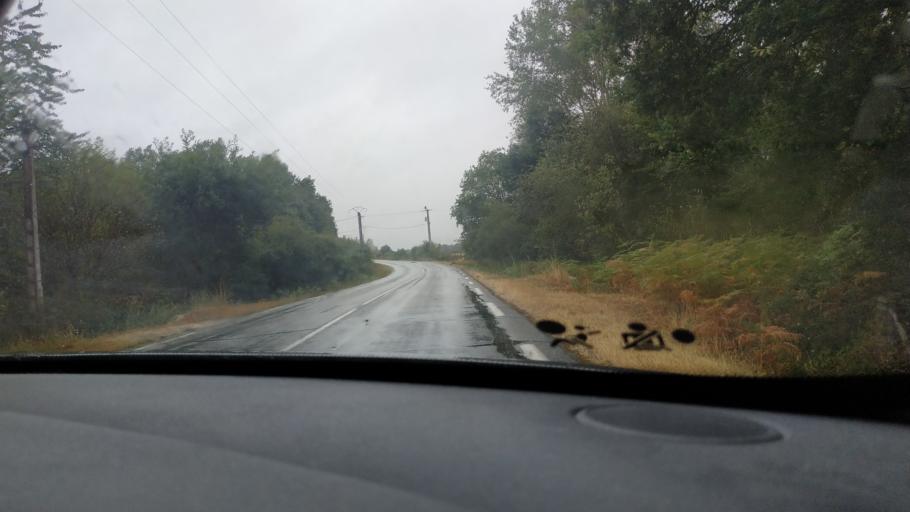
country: FR
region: Centre
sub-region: Departement du Loiret
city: Bellegarde
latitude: 47.9372
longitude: 2.3880
